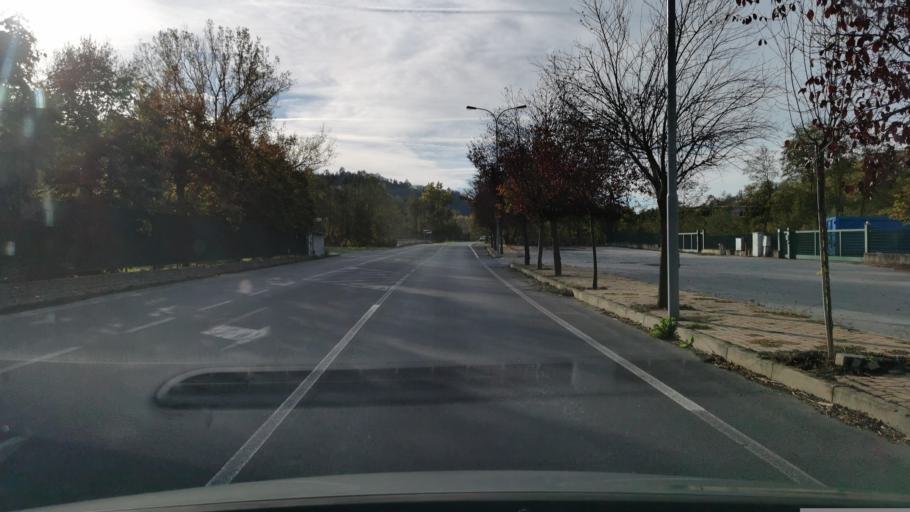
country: IT
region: Piedmont
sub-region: Provincia di Cuneo
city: Monchiero Borgonuovo
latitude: 44.5628
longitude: 7.9222
